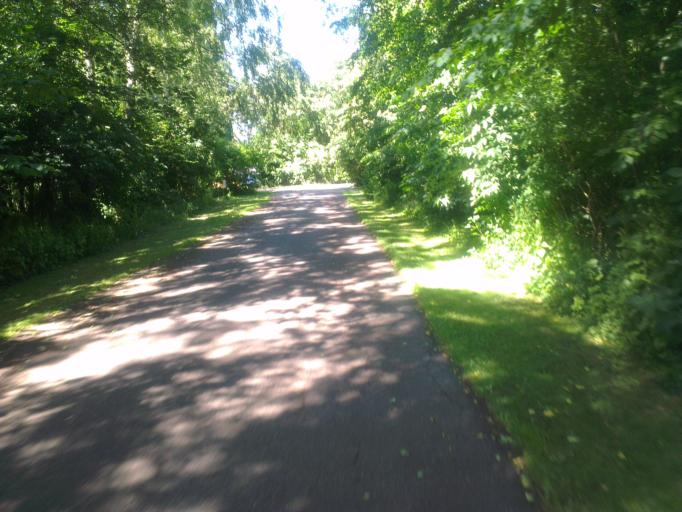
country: DK
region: Capital Region
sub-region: Halsnaes Kommune
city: Hundested
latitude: 55.9141
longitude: 11.9174
